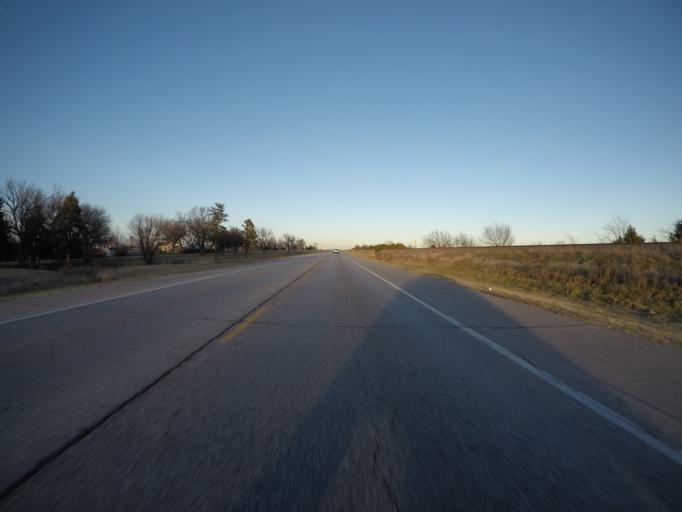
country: US
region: Kansas
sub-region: Harvey County
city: North Newton
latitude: 38.1203
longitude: -97.2529
